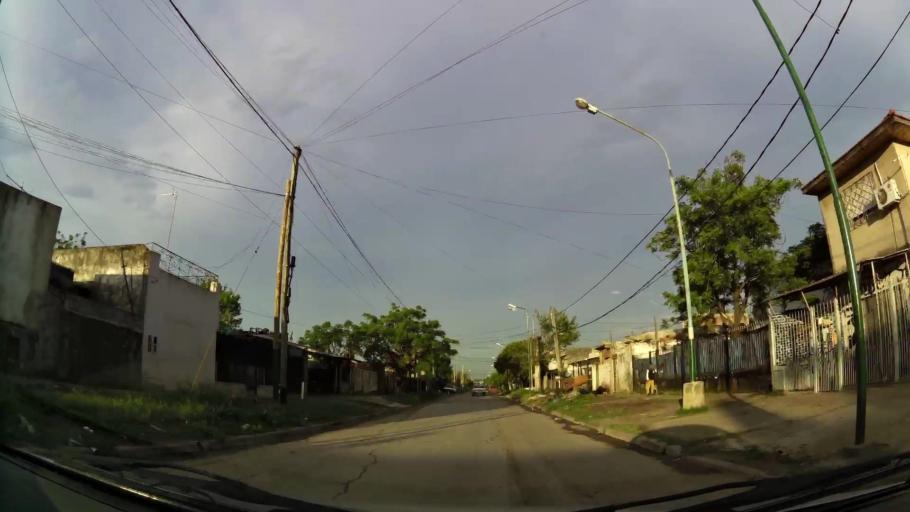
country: AR
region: Buenos Aires
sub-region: Partido de Almirante Brown
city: Adrogue
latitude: -34.7740
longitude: -58.3474
